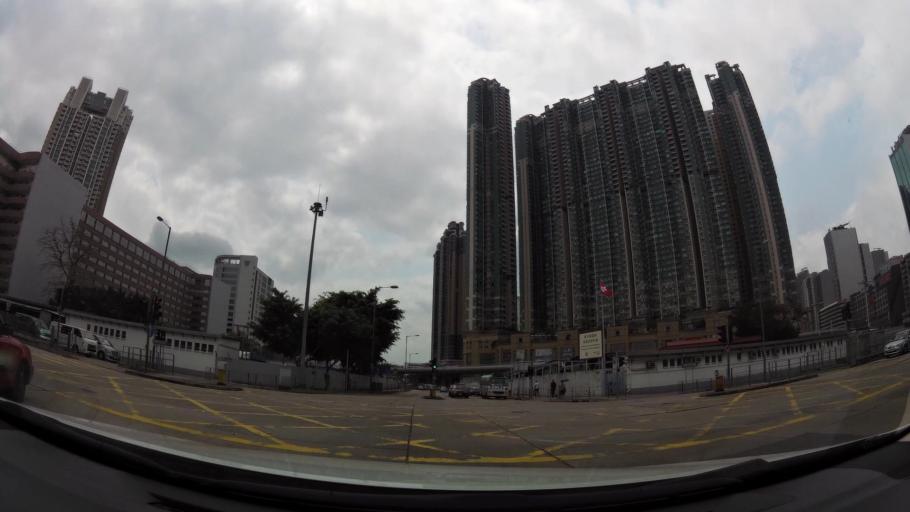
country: HK
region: Sham Shui Po
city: Sham Shui Po
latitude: 22.3355
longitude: 114.1518
